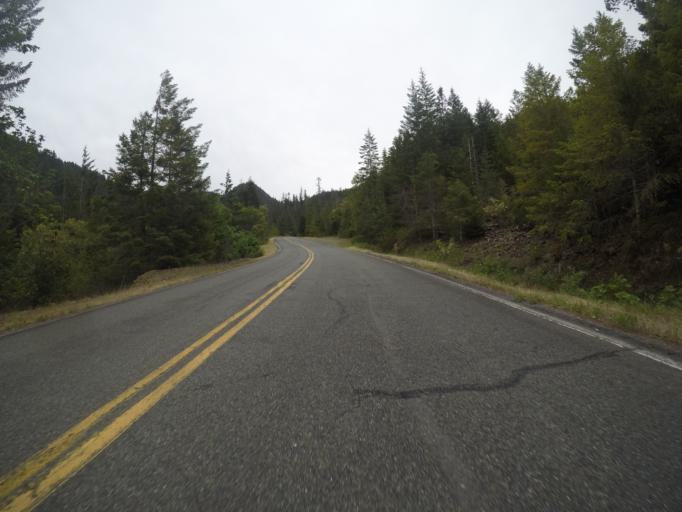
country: US
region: California
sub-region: Del Norte County
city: Bertsch-Oceanview
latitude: 41.7053
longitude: -123.9396
